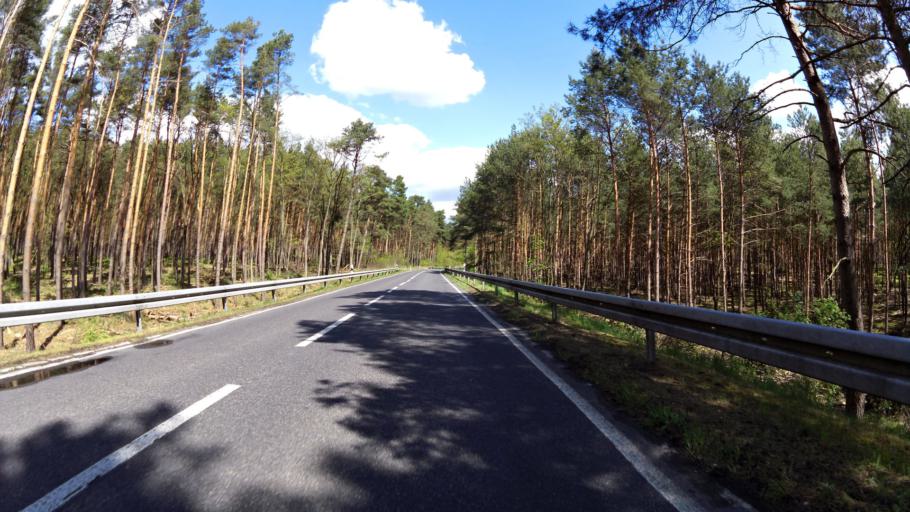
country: DE
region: Brandenburg
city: Wendisch Rietz
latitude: 52.1482
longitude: 13.9727
